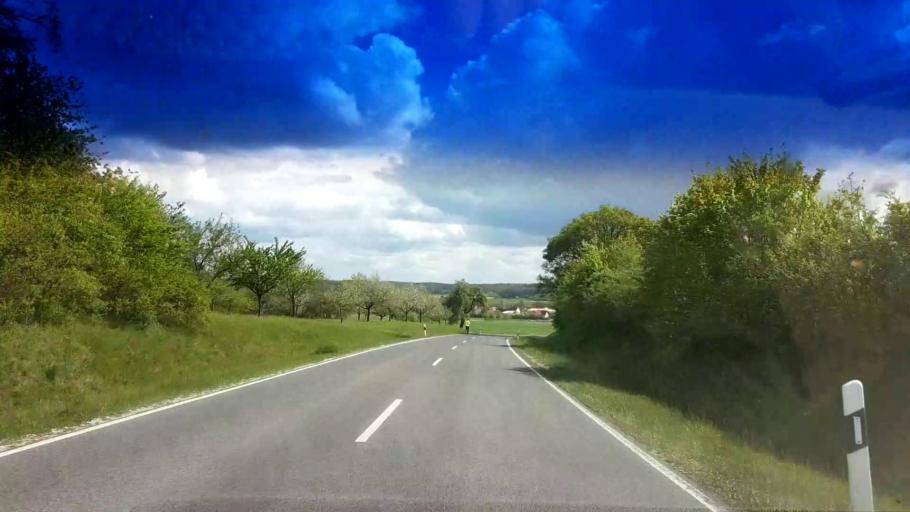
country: DE
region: Bavaria
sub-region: Upper Franconia
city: Frensdorf
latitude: 49.8321
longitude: 10.8405
